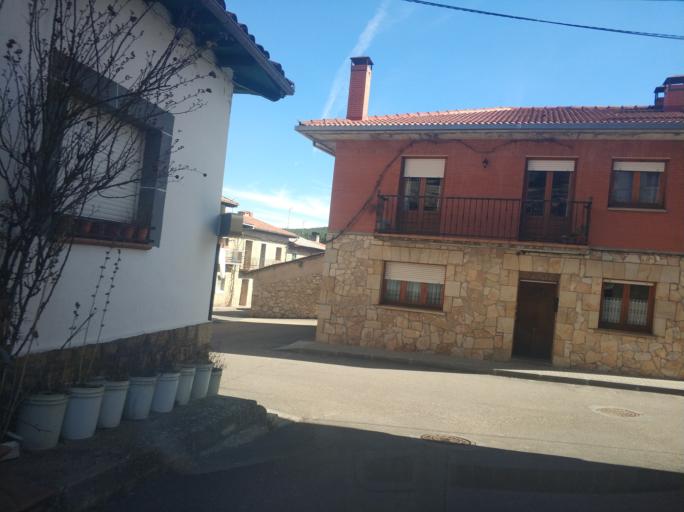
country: ES
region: Castille and Leon
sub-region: Provincia de Soria
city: San Leonardo de Yague
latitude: 41.8298
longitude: -3.0705
